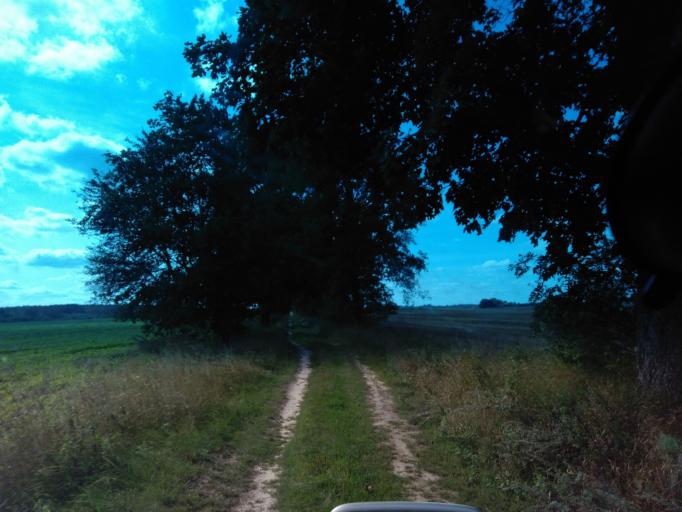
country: BY
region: Minsk
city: Stan'kava
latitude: 53.6340
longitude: 27.3243
